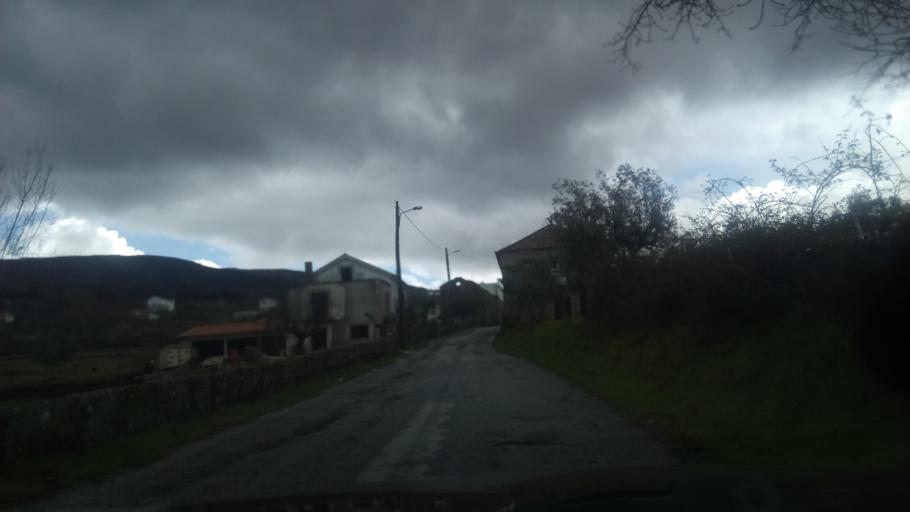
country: PT
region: Guarda
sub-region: Celorico da Beira
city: Celorico da Beira
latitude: 40.5586
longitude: -7.4570
